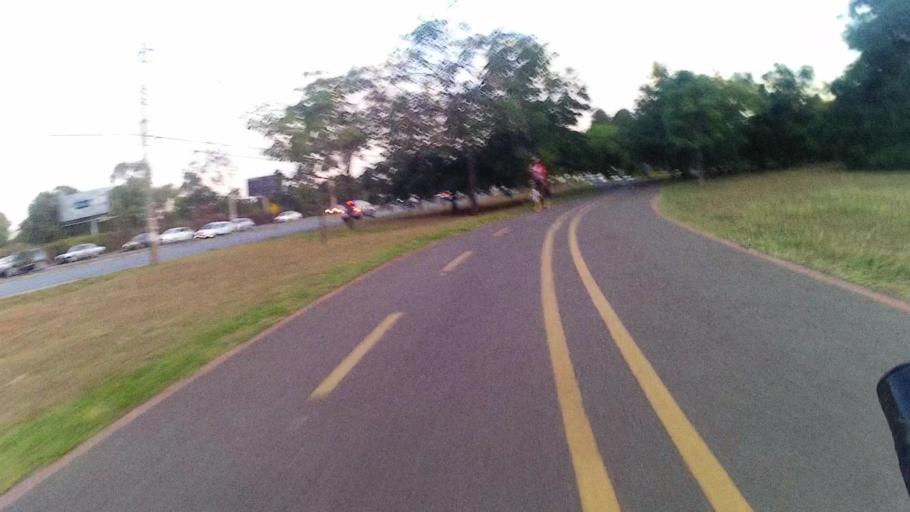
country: BR
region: Federal District
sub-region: Brasilia
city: Brasilia
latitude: -15.8277
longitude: -48.0085
